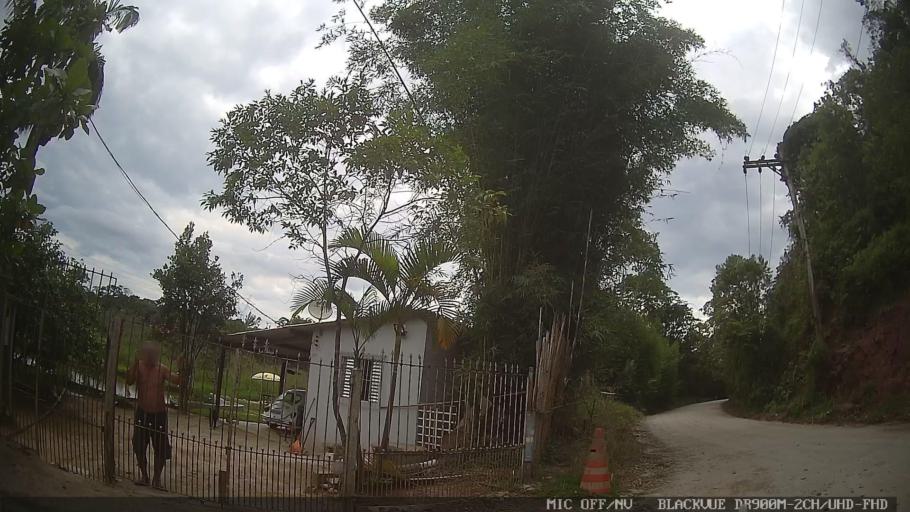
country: BR
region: Sao Paulo
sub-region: Rio Grande Da Serra
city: Rio Grande da Serra
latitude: -23.6968
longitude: -46.2881
